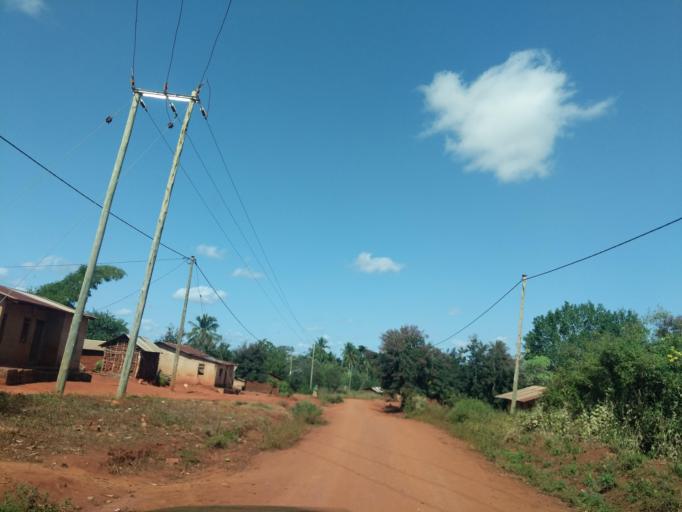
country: TZ
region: Tanga
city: Muheza
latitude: -5.3844
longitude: 38.5792
